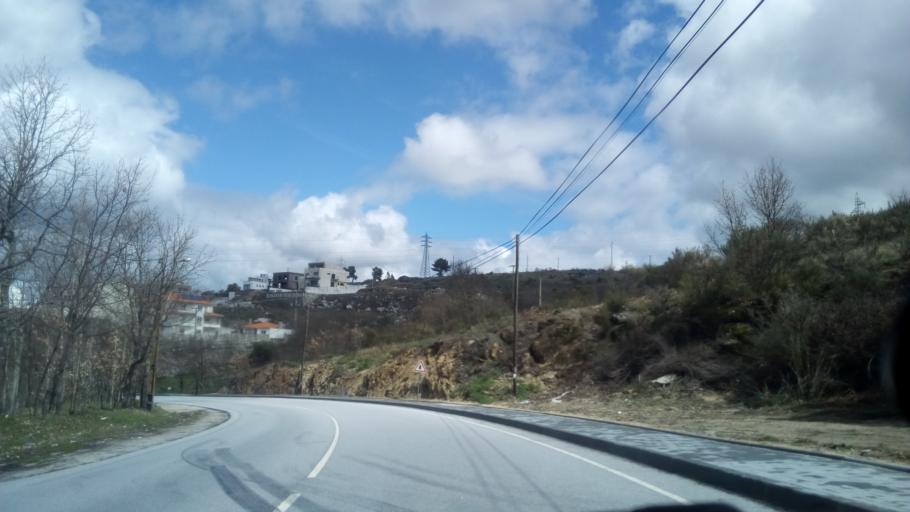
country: PT
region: Guarda
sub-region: Guarda
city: Guarda
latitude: 40.5370
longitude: -7.2917
